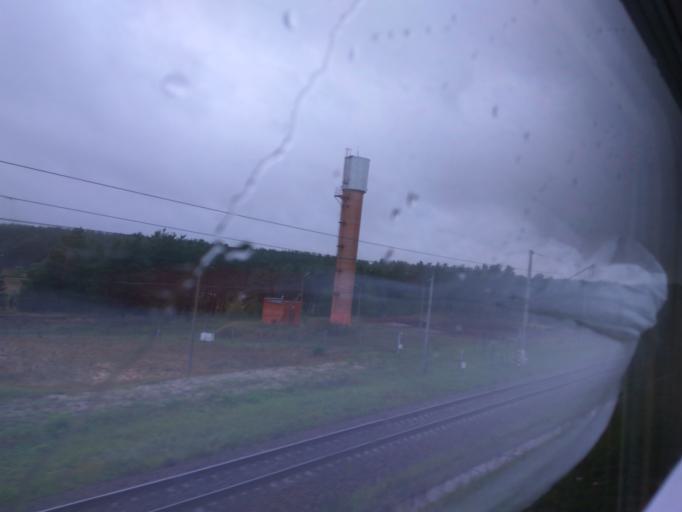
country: RU
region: Moskovskaya
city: Kashira
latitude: 54.8643
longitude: 38.1606
